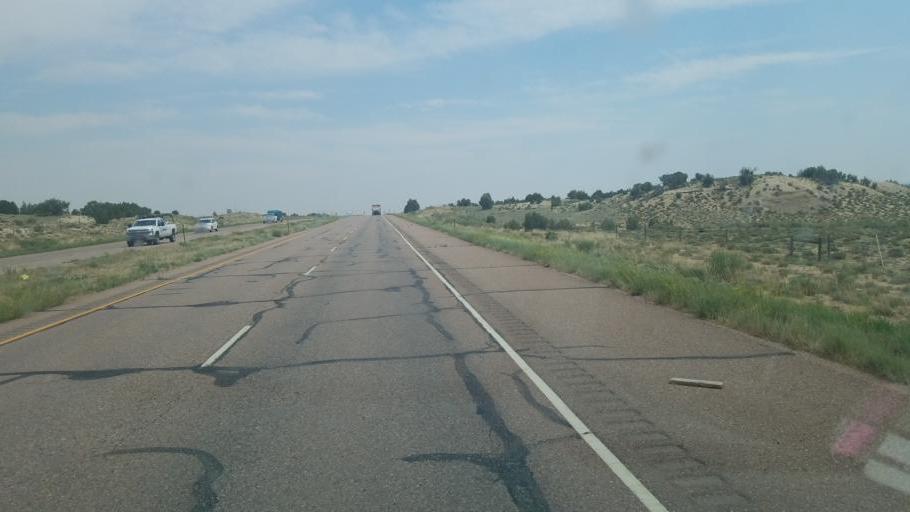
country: US
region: Colorado
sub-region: Fremont County
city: Penrose
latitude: 38.3967
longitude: -104.9756
